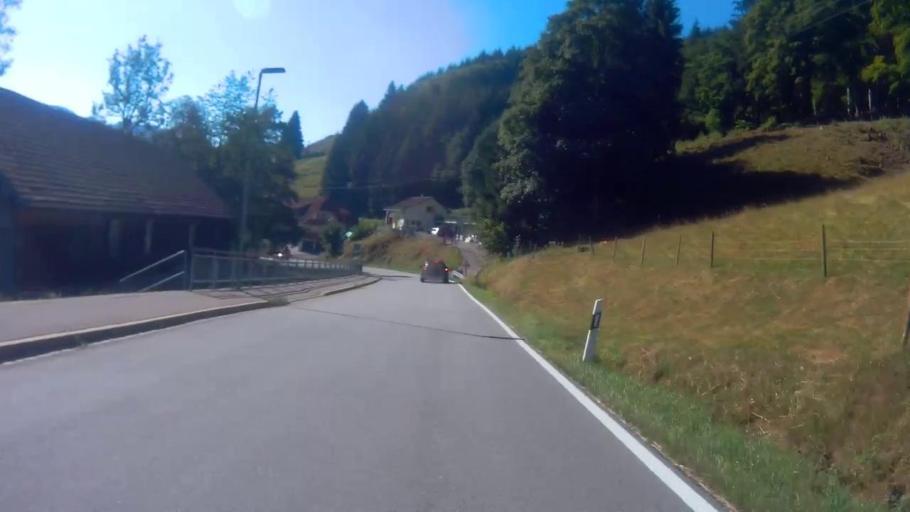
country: DE
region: Baden-Wuerttemberg
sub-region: Freiburg Region
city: Aitern
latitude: 47.8045
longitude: 7.8905
